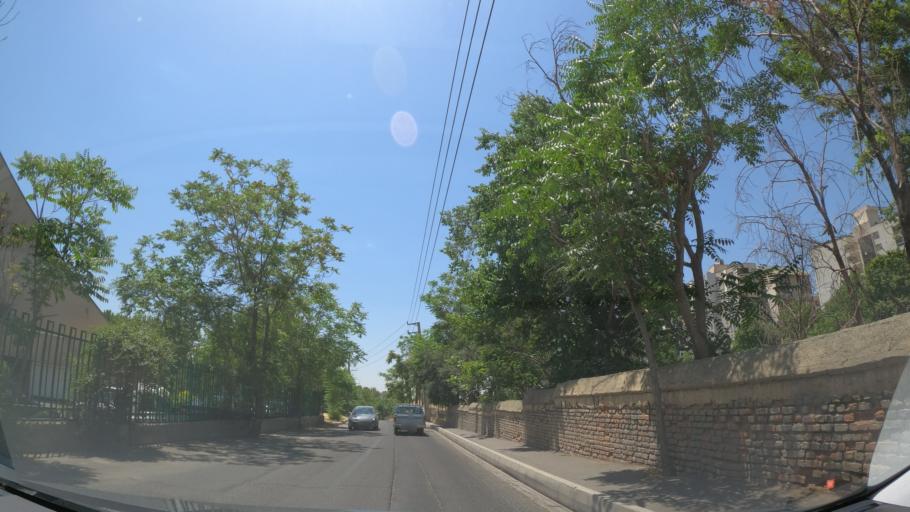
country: IR
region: Tehran
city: Tajrish
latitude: 35.7836
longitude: 51.3889
